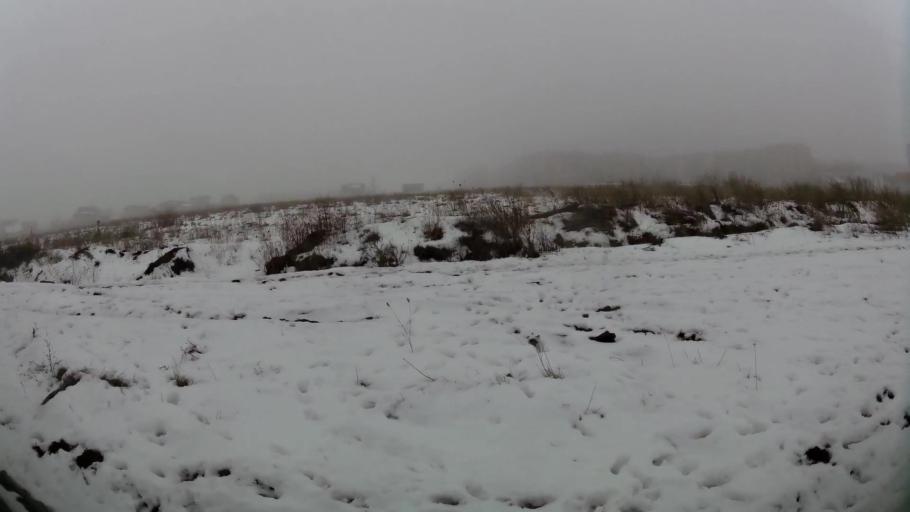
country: RO
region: Ilfov
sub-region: Comuna Chiajna
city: Rosu
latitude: 44.4415
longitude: 25.9933
